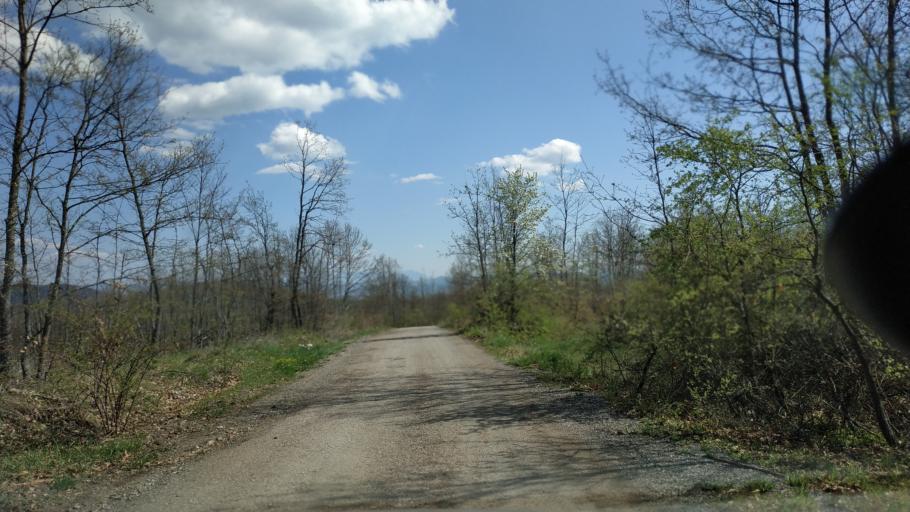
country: RS
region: Central Serbia
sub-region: Zajecarski Okrug
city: Soko Banja
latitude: 43.5486
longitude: 21.8993
